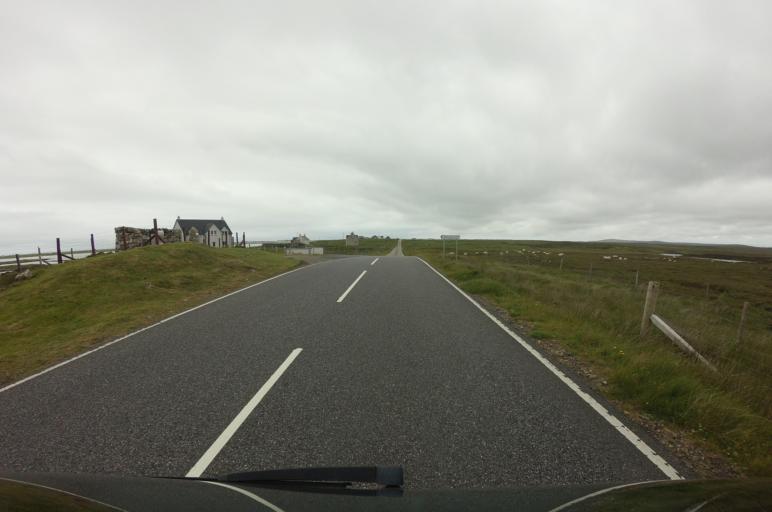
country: GB
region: Scotland
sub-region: Eilean Siar
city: Isle of North Uist
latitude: 57.5554
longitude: -7.3461
